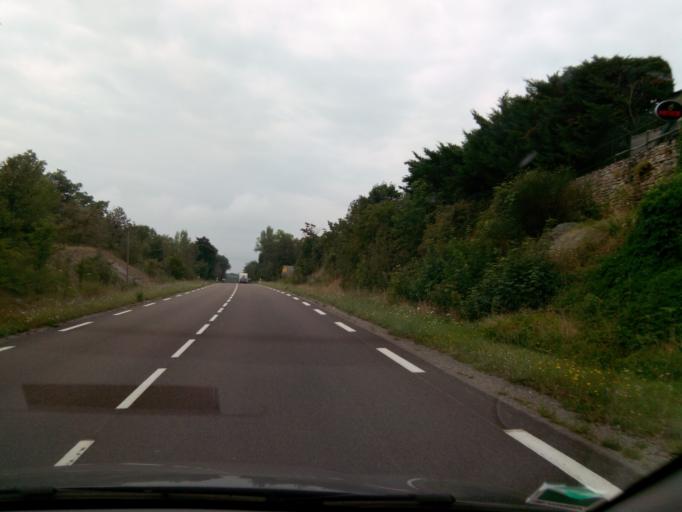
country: FR
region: Midi-Pyrenees
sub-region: Departement du Lot
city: Souillac
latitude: 44.9488
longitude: 1.4949
